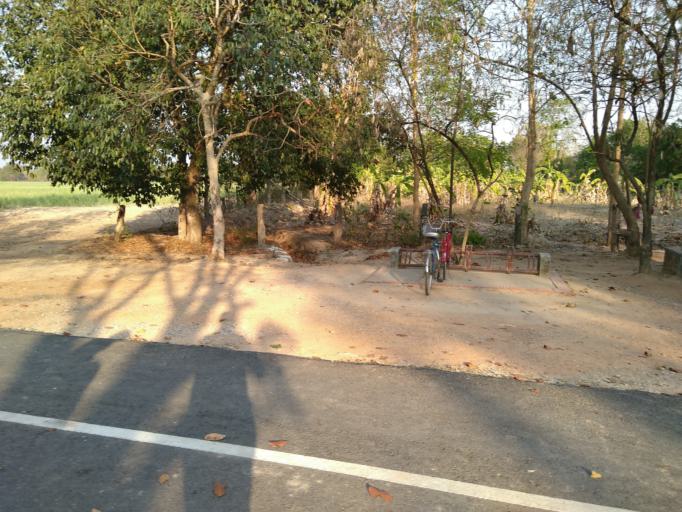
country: TH
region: Sukhothai
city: Ban Na
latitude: 17.0230
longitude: 99.6769
